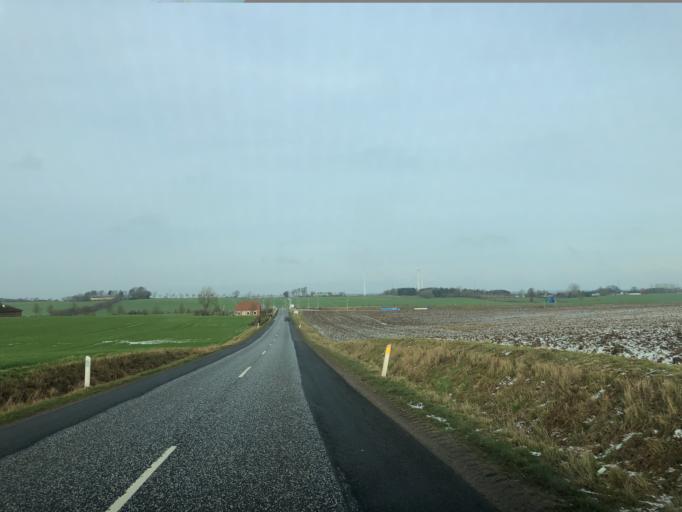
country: DK
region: Central Jutland
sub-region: Hedensted Kommune
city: Torring
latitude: 55.8281
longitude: 9.4746
